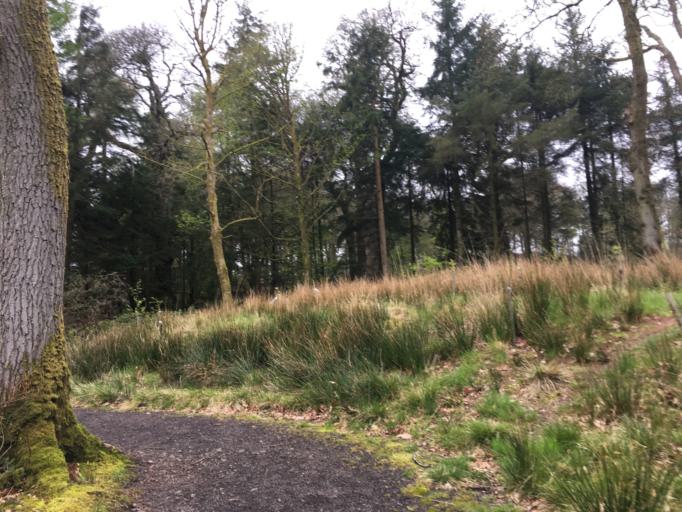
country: GB
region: Scotland
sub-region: Argyll and Bute
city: Rothesay
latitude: 55.7998
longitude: -5.0253
